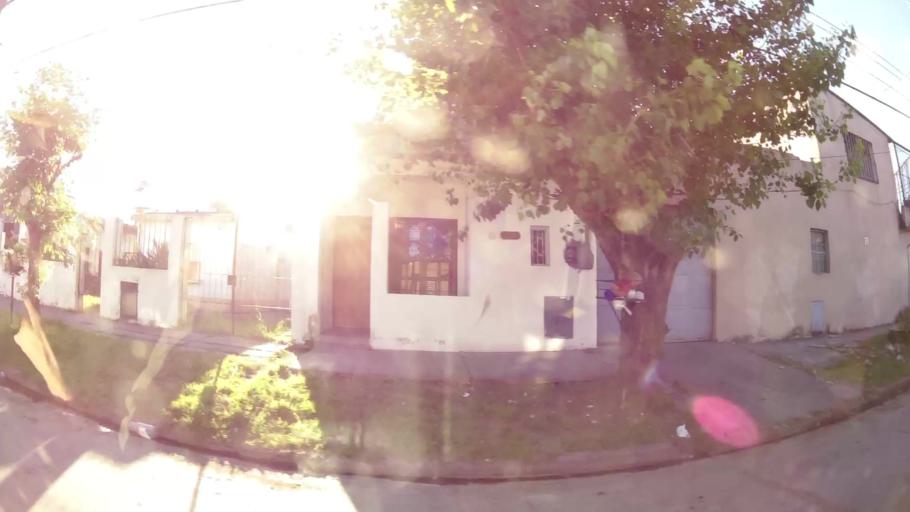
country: AR
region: Buenos Aires
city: Ituzaingo
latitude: -34.6881
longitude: -58.6395
